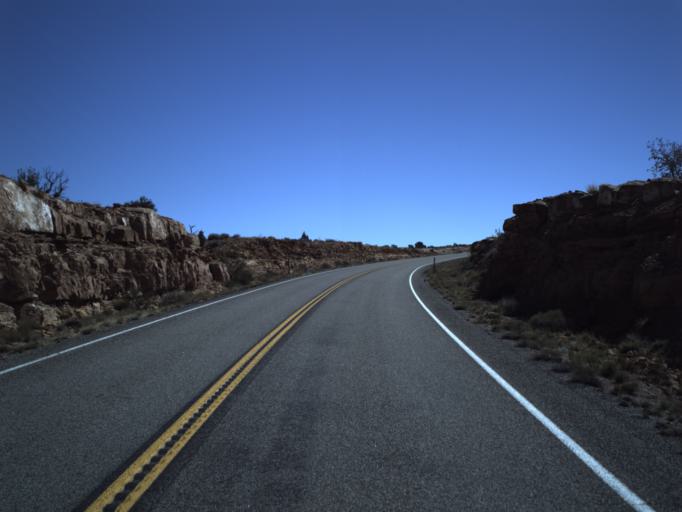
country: US
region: Utah
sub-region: San Juan County
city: Blanding
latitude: 37.8197
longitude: -110.3496
